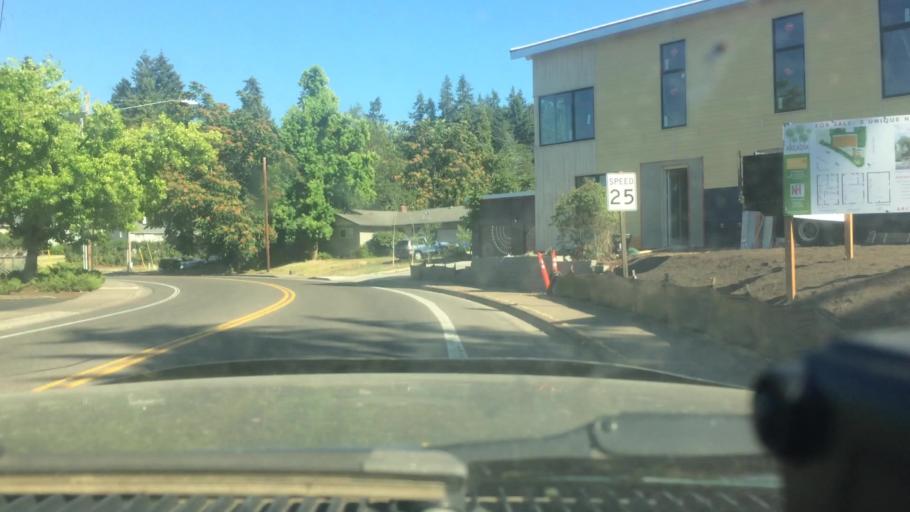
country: US
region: Oregon
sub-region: Lane County
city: Eugene
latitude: 44.0276
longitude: -123.1054
